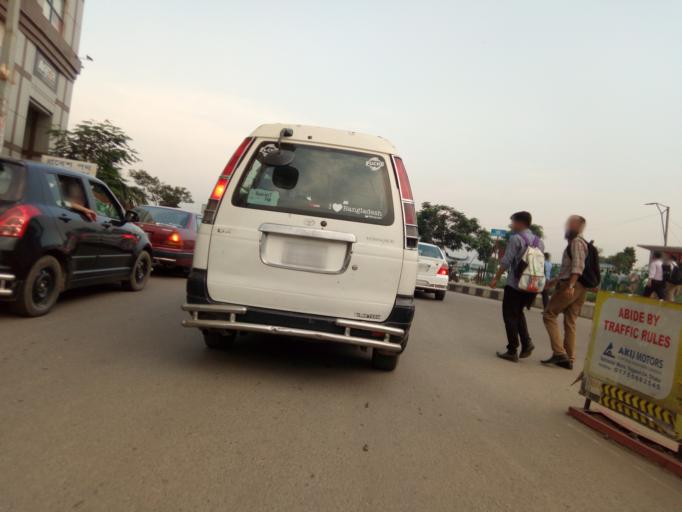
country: BD
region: Dhaka
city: Paltan
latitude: 23.7730
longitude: 90.4158
